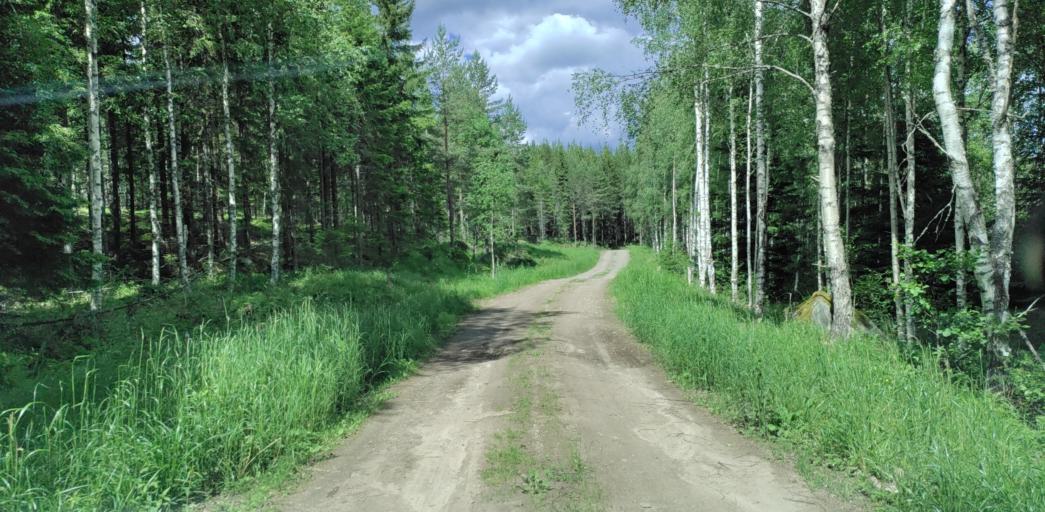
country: SE
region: Vaermland
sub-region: Hagfors Kommun
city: Ekshaerad
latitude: 60.1174
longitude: 13.3259
